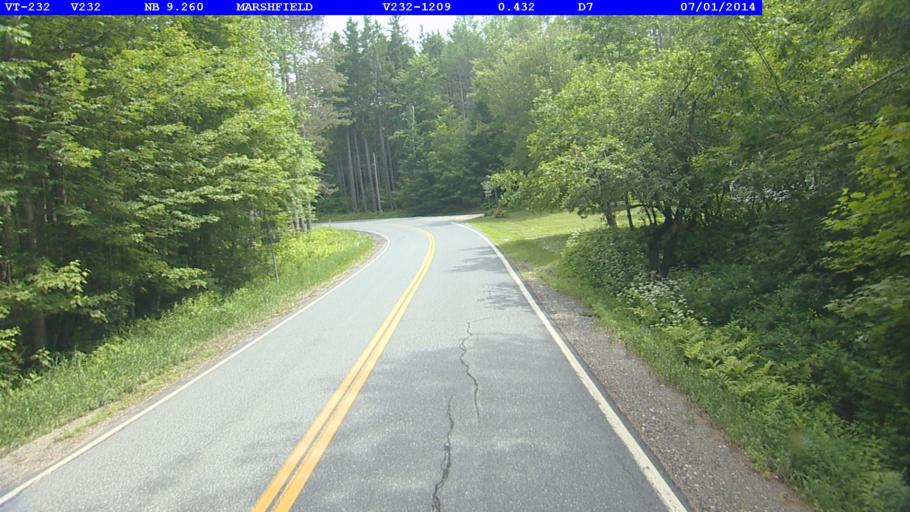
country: US
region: Vermont
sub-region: Caledonia County
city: Hardwick
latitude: 44.3223
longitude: -72.2901
